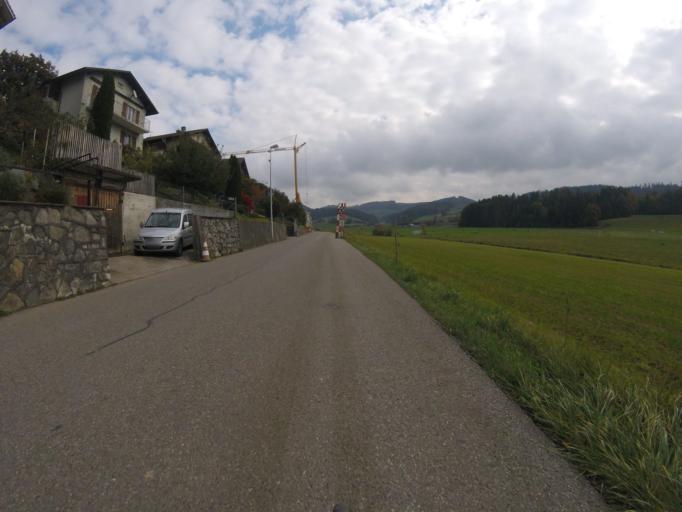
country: CH
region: Bern
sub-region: Bern-Mittelland District
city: Koniz
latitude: 46.8976
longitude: 7.3932
